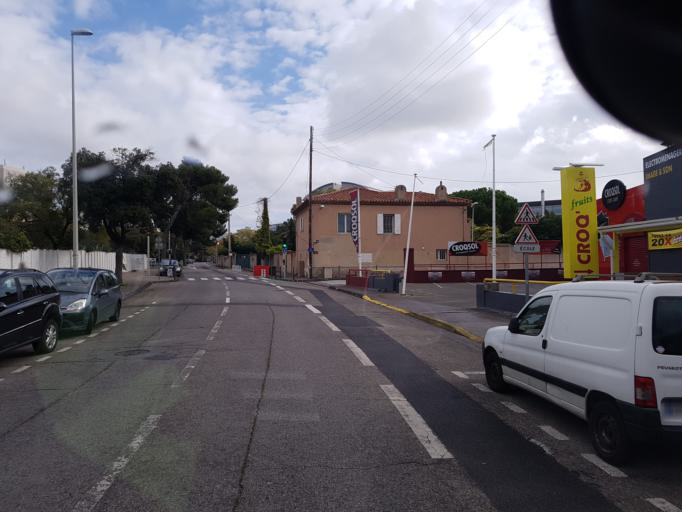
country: FR
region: Provence-Alpes-Cote d'Azur
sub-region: Departement des Bouches-du-Rhone
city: Marseille 09
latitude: 43.2461
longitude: 5.3902
